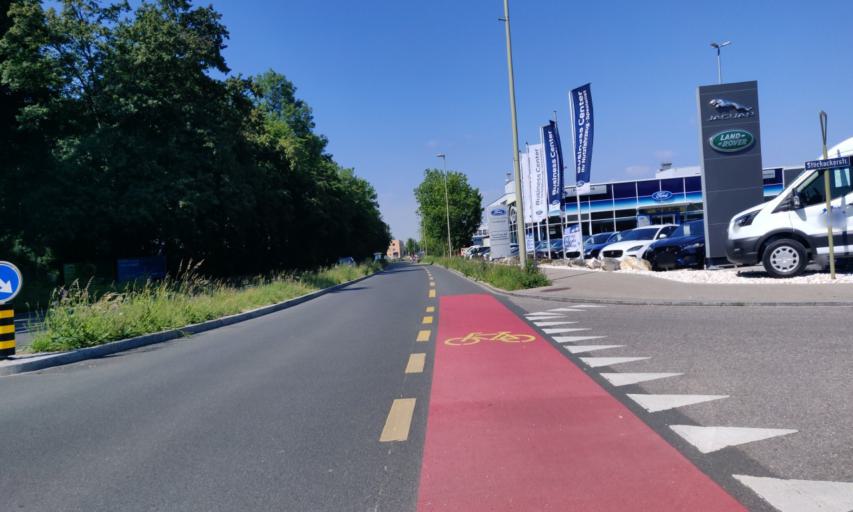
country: CH
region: Basel-Landschaft
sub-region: Bezirk Arlesheim
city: Munchenstein
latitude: 47.5213
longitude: 7.6032
